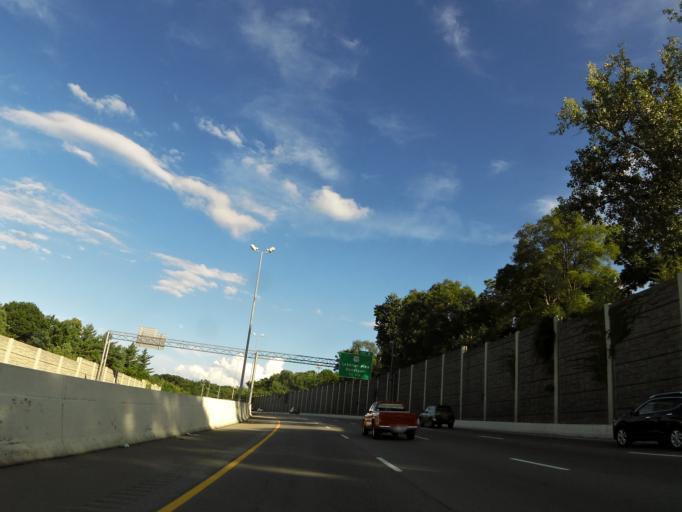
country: US
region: Tennessee
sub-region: Davidson County
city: Lakewood
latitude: 36.1770
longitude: -86.6946
